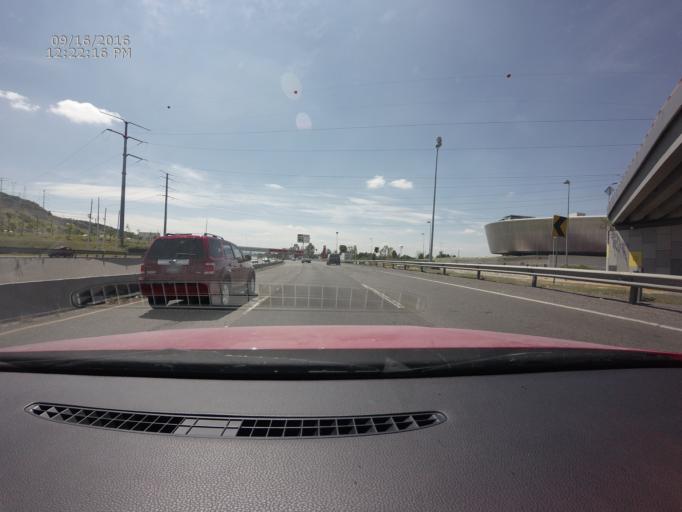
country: MX
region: Queretaro
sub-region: Queretaro
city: Sergio Villasenor
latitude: 20.6408
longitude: -100.4306
